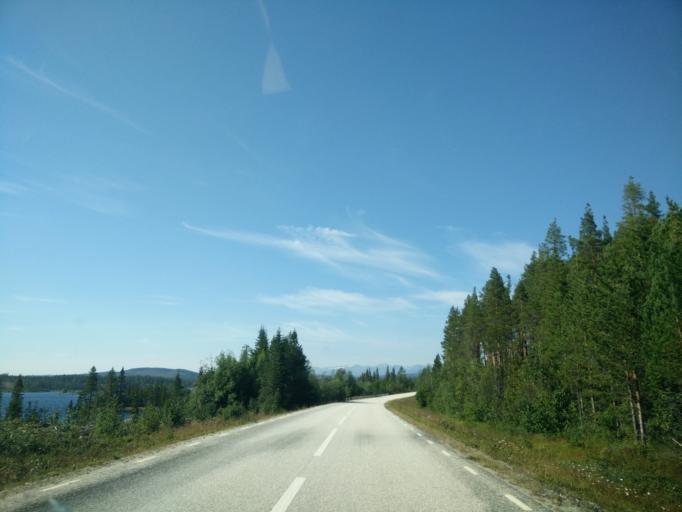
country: SE
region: Jaemtland
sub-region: Are Kommun
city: Jarpen
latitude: 62.8094
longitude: 13.5291
